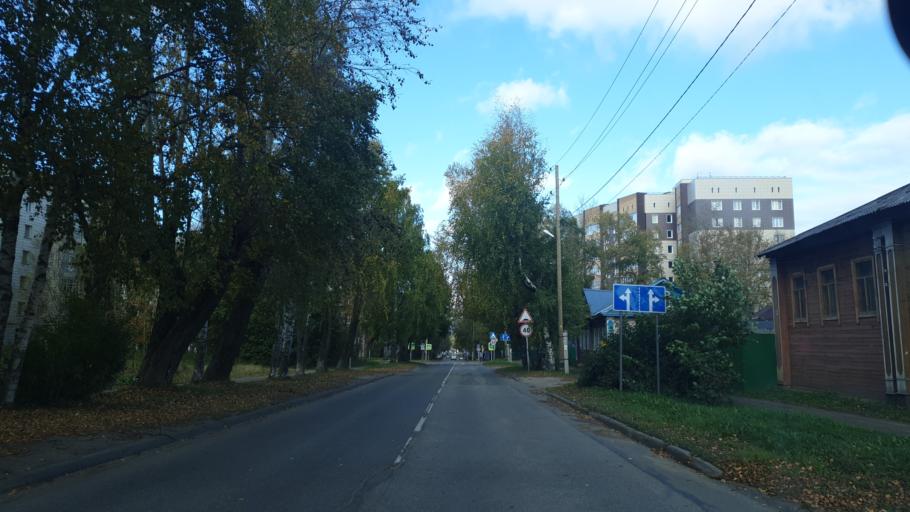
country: RU
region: Komi Republic
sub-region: Syktyvdinskiy Rayon
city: Syktyvkar
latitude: 61.6616
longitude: 50.8411
